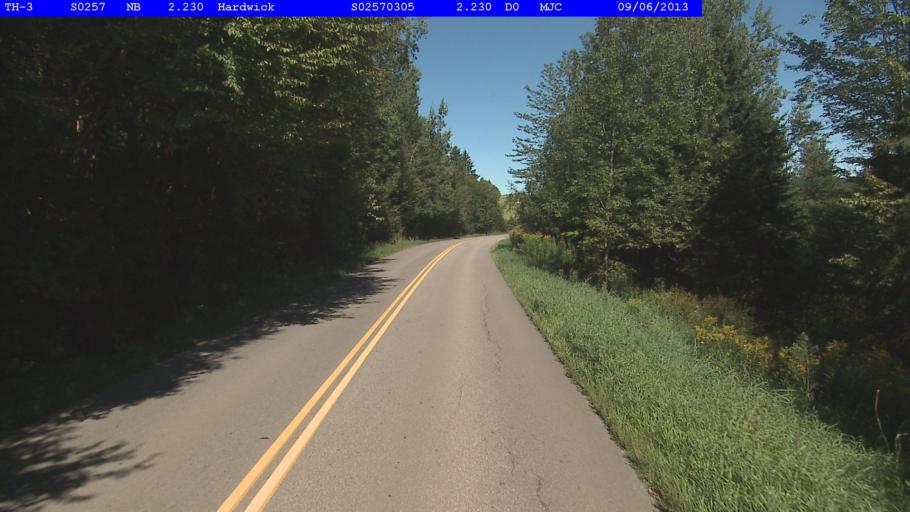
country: US
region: Vermont
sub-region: Caledonia County
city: Hardwick
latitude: 44.5232
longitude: -72.3406
